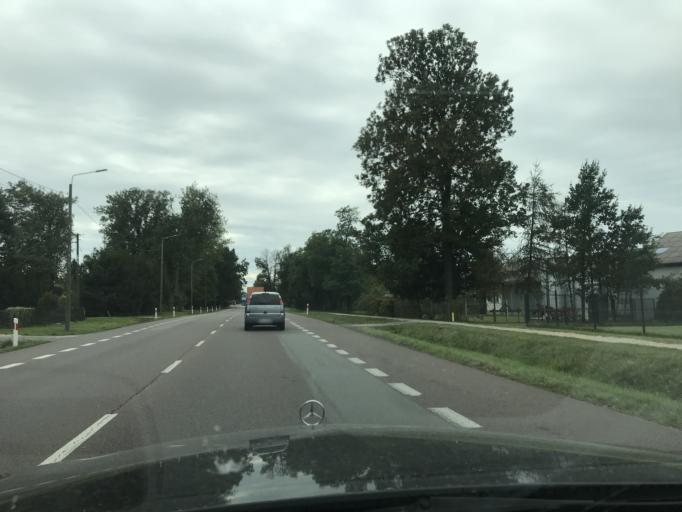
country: PL
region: Lublin Voivodeship
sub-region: Powiat krasnicki
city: Wilkolaz
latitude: 51.0065
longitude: 22.3421
